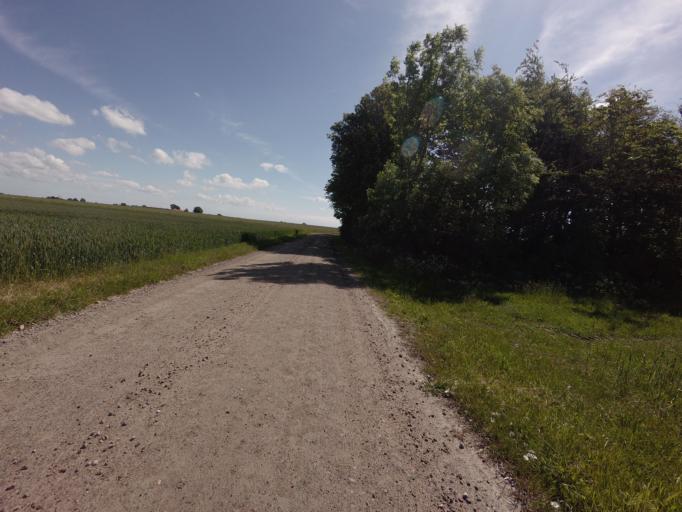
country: SE
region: Skane
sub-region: Trelleborgs Kommun
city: Skare
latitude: 55.4138
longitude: 13.0490
